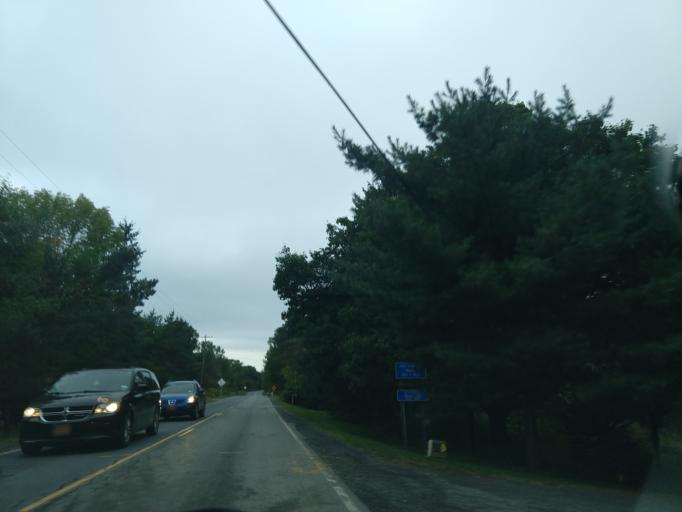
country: US
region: New York
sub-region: Tompkins County
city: East Ithaca
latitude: 42.4049
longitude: -76.4655
